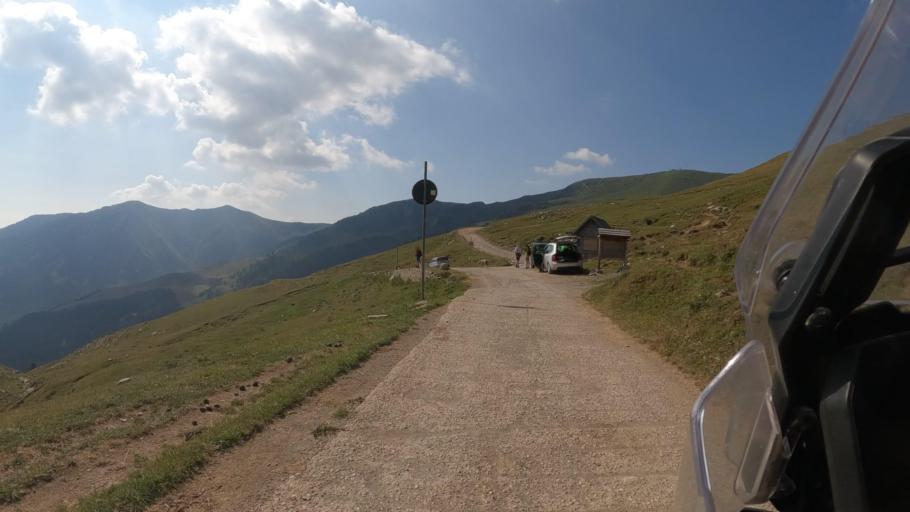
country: IT
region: Piedmont
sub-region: Provincia di Cuneo
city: Briga Alta
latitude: 44.0767
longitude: 7.7209
